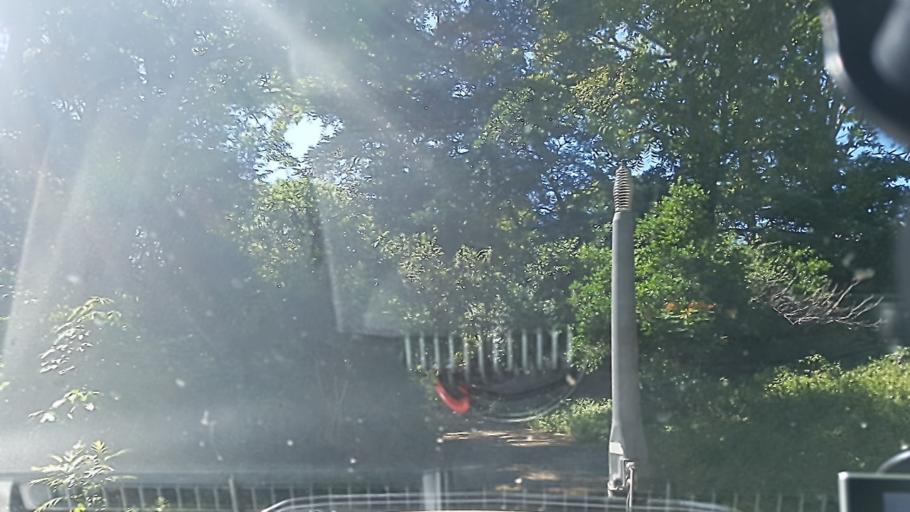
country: NI
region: Rivas
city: Tola
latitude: 11.5418
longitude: -86.1000
